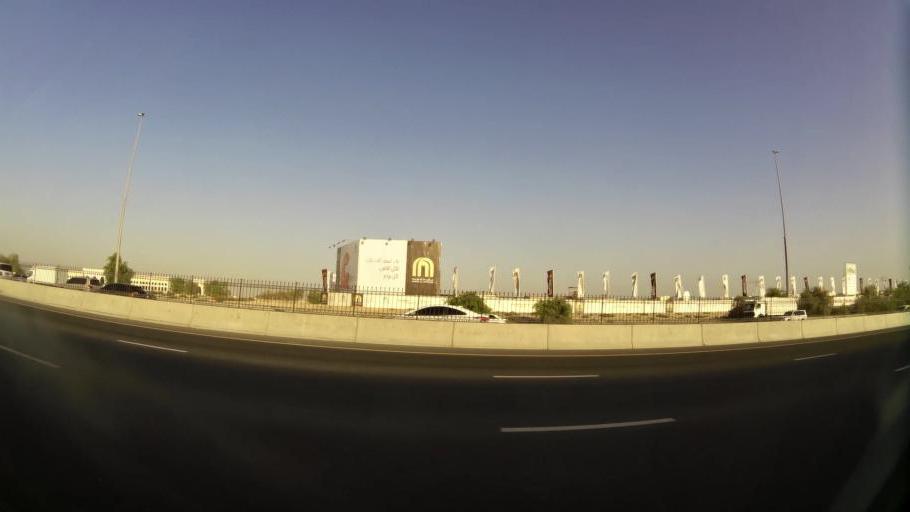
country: AE
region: Ash Shariqah
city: Sharjah
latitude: 25.3195
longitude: 55.4538
